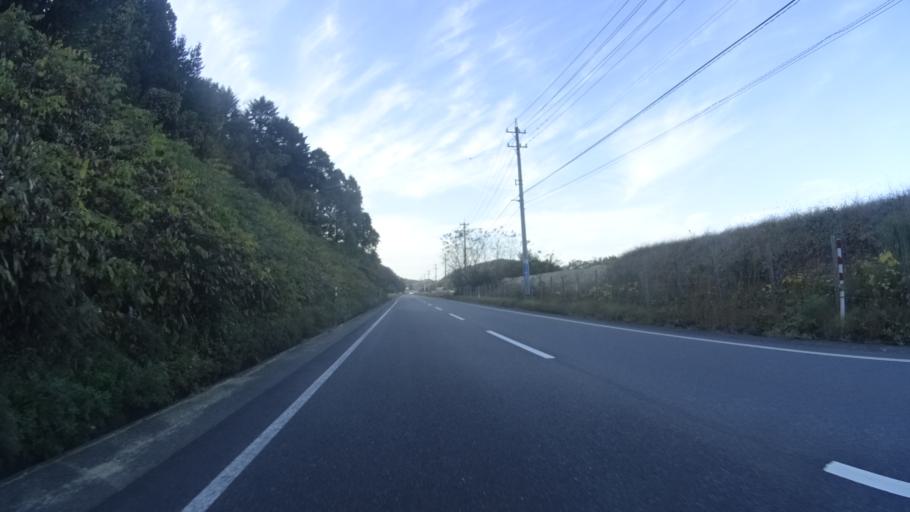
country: JP
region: Ishikawa
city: Hakui
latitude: 37.0168
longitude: 136.7942
